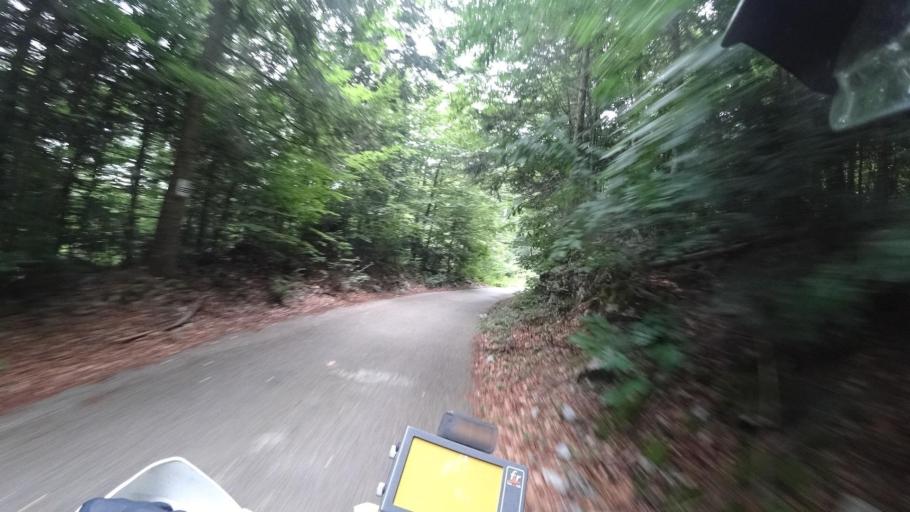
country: HR
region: Licko-Senjska
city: Senj
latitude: 45.1114
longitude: 14.9466
